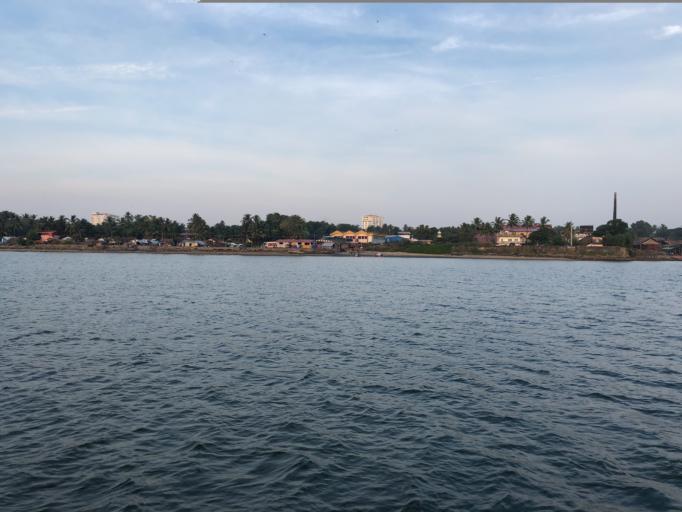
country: IN
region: Karnataka
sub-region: Dakshina Kannada
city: Ullal
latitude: 12.8463
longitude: 74.8354
